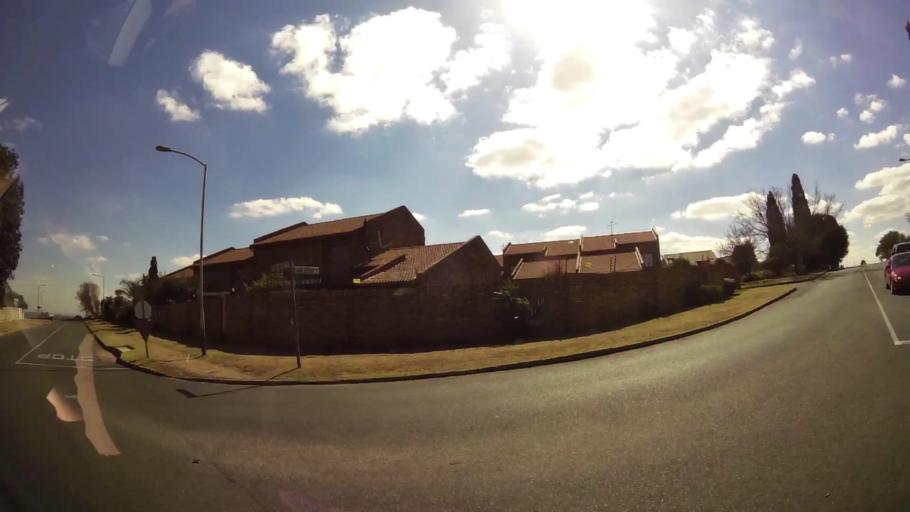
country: ZA
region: Gauteng
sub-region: West Rand District Municipality
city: Krugersdorp
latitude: -26.1021
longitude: 27.7953
